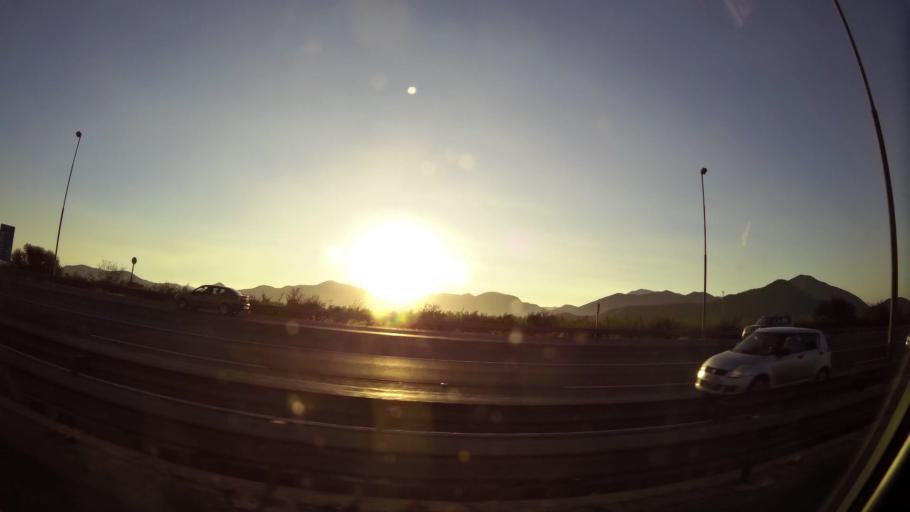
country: CL
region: Santiago Metropolitan
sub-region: Provincia de Santiago
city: Lo Prado
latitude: -33.5046
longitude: -70.7992
